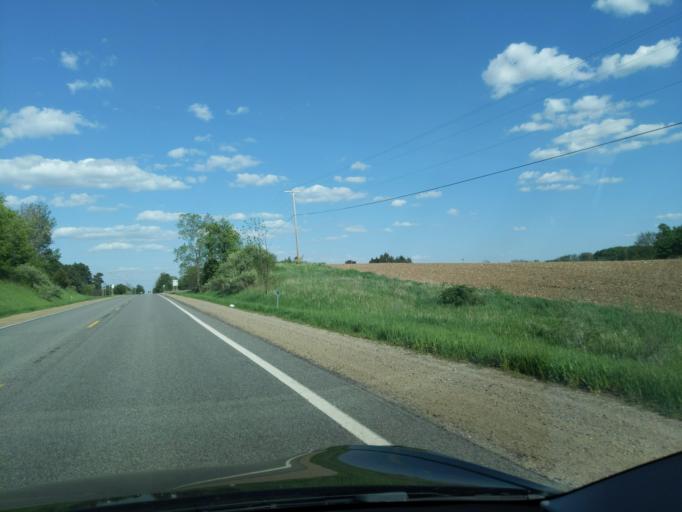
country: US
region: Michigan
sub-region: Ionia County
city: Portland
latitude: 42.7556
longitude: -84.9387
